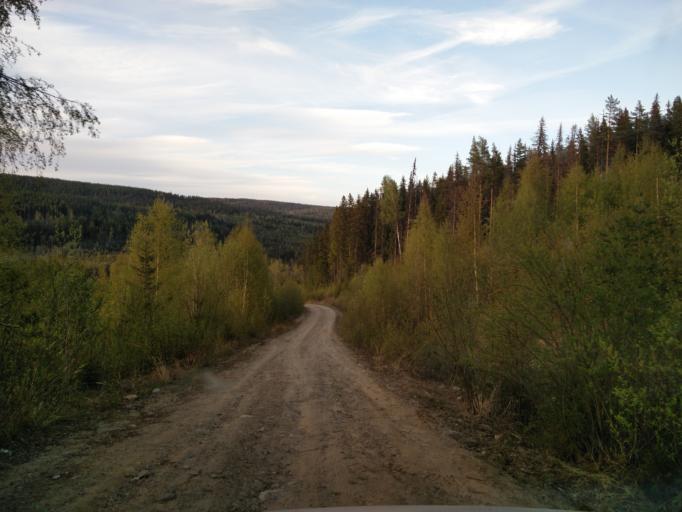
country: SE
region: Vaesternorrland
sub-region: Sundsvalls Kommun
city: Matfors
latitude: 62.3996
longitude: 16.8175
